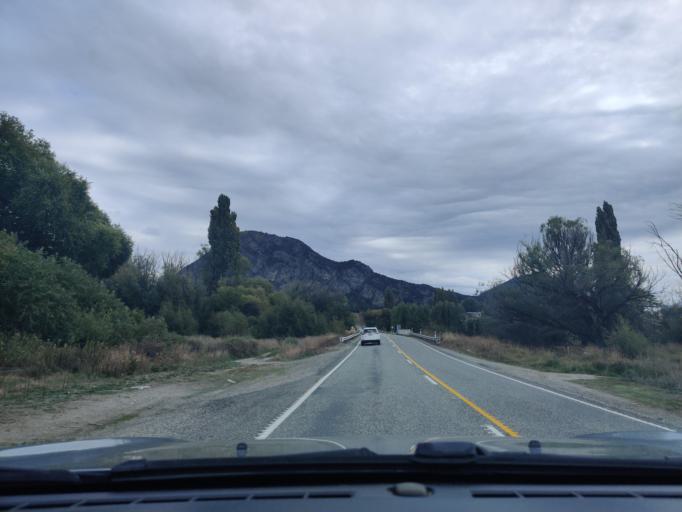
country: NZ
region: Otago
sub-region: Queenstown-Lakes District
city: Wanaka
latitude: -44.6998
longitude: 169.1783
